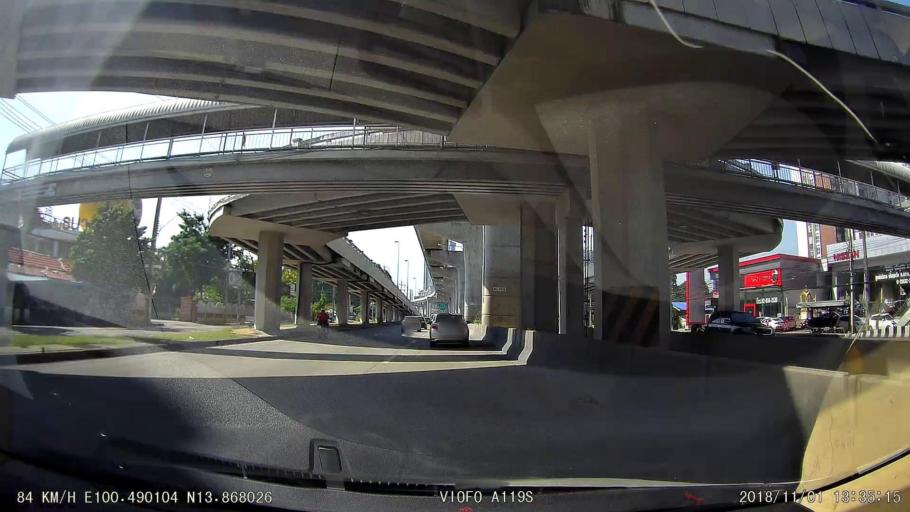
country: TH
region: Nonthaburi
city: Mueang Nonthaburi
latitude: 13.8680
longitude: 100.4900
